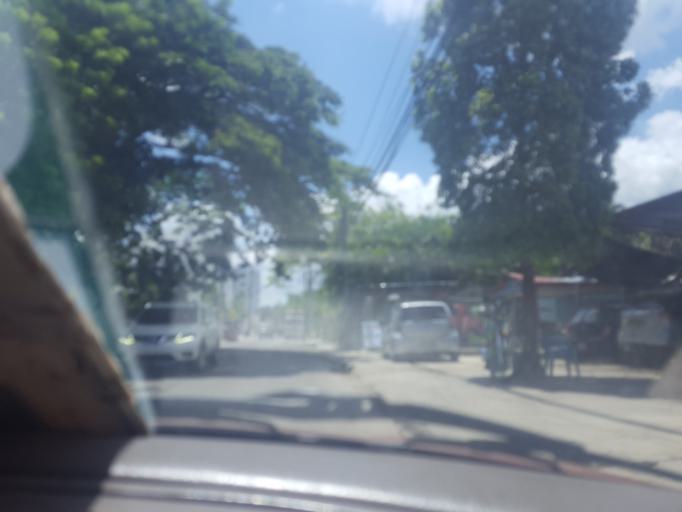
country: DO
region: Santiago
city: Santiago de los Caballeros
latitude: 19.4712
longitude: -70.6648
